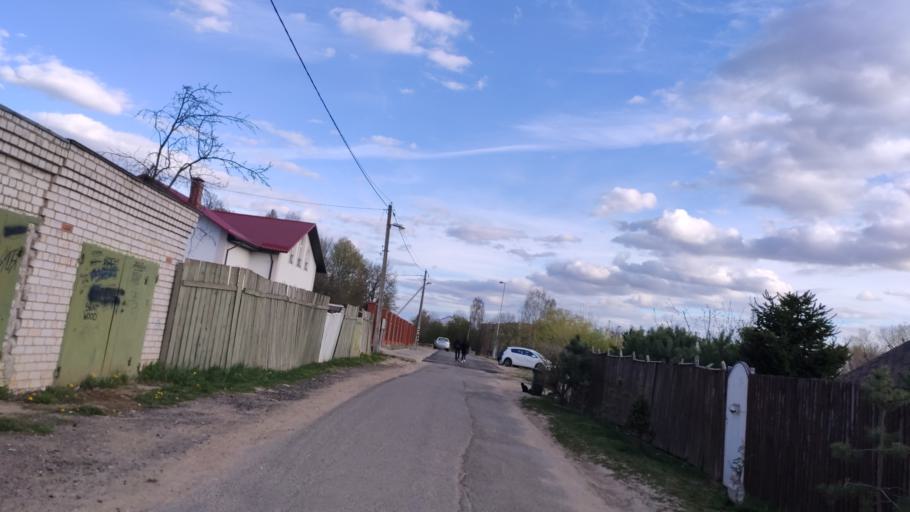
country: BY
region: Minsk
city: Minsk
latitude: 53.8991
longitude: 27.5175
